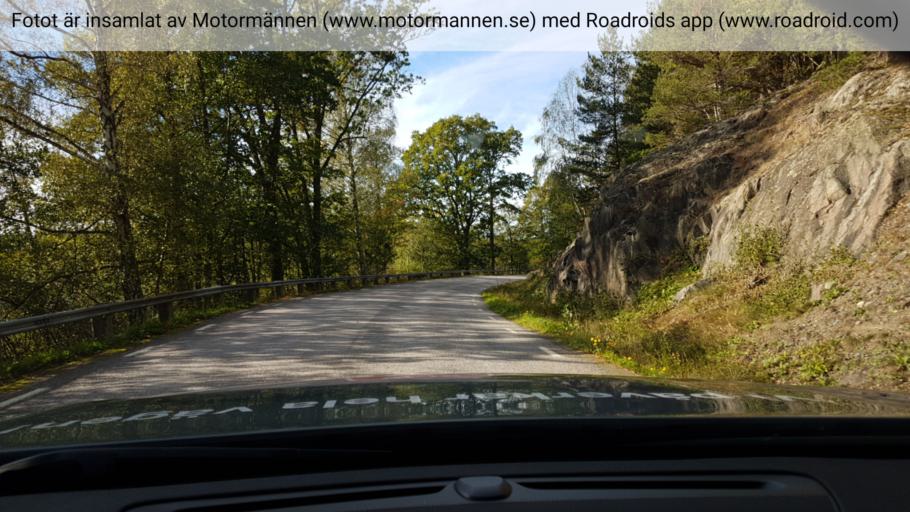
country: SE
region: OEstergoetland
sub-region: Valdemarsviks Kommun
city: Valdemarsvik
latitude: 58.1357
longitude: 16.6184
